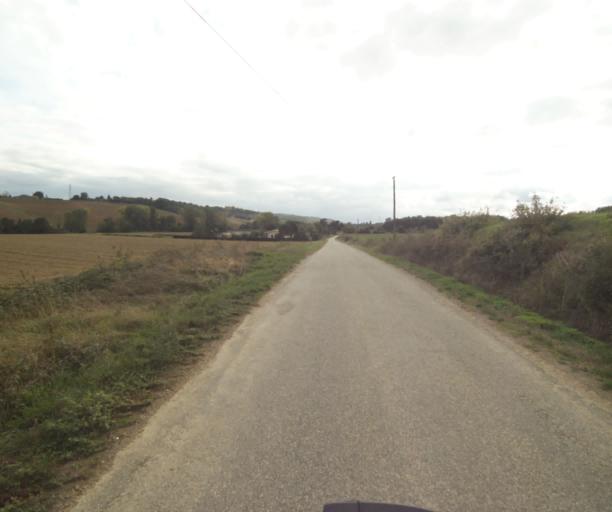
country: FR
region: Midi-Pyrenees
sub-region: Departement du Tarn-et-Garonne
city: Verdun-sur-Garonne
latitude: 43.8561
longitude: 1.1254
